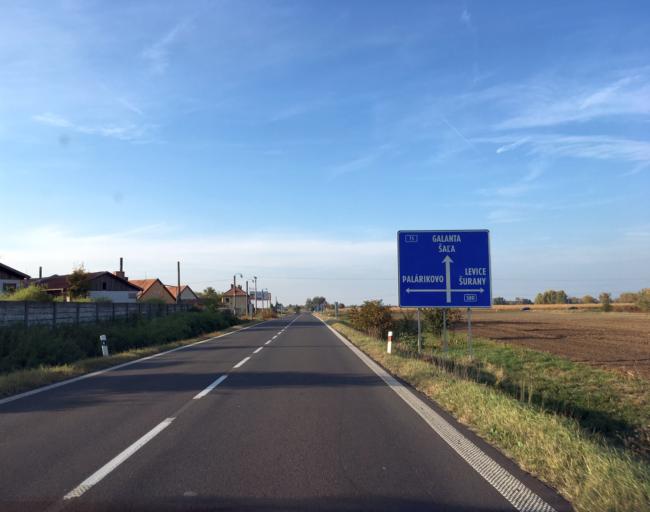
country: SK
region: Nitriansky
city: Surany
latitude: 48.0604
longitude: 18.1012
